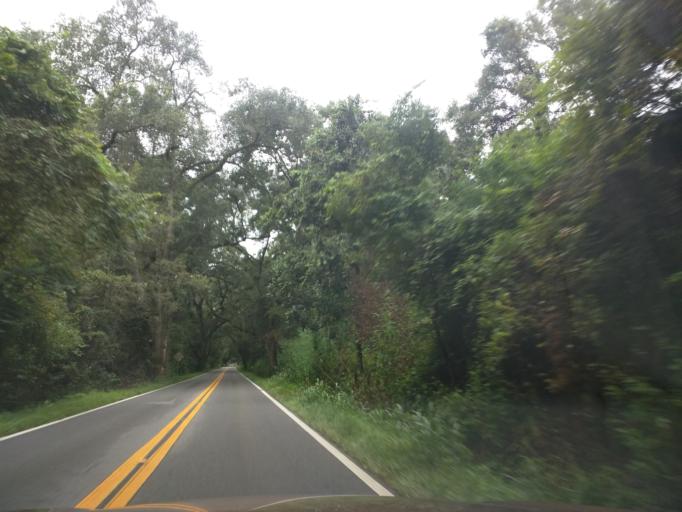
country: US
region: Florida
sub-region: Leon County
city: Tallahassee
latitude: 30.4861
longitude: -84.1947
